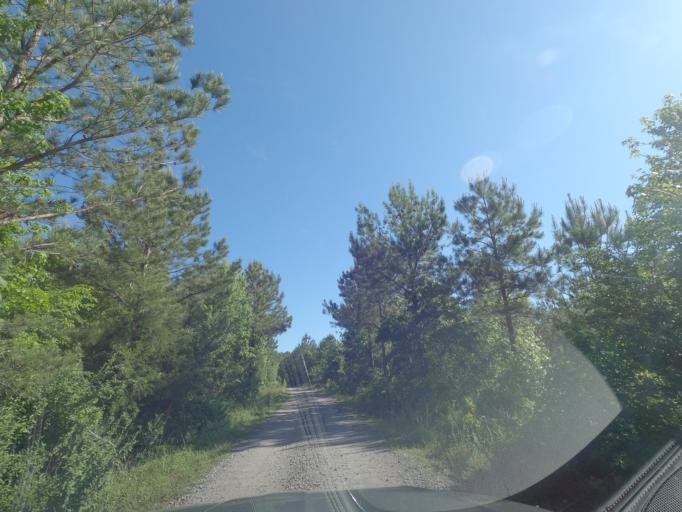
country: US
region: Georgia
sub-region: Columbia County
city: Evans
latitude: 33.6094
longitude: -82.1131
